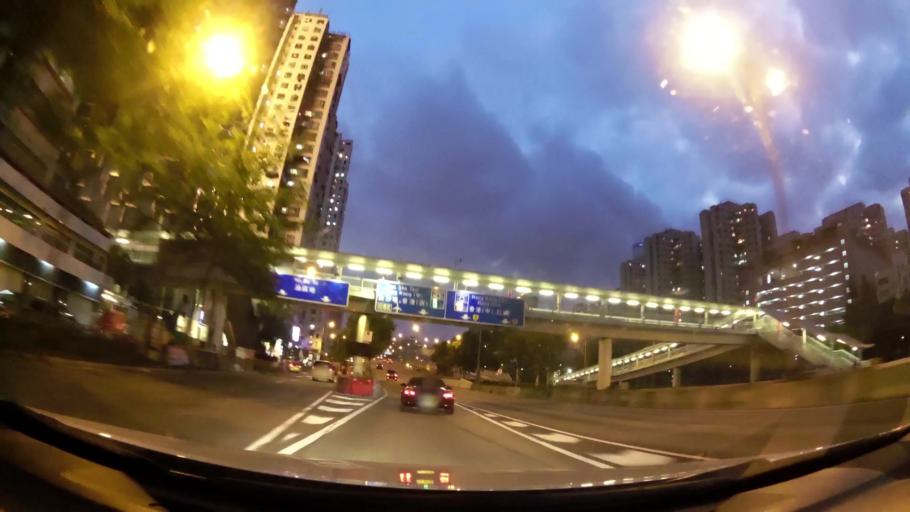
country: HK
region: Sham Shui Po
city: Sham Shui Po
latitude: 22.3156
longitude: 114.1669
